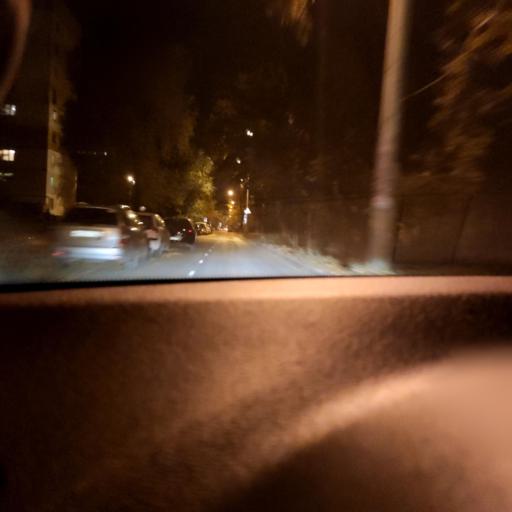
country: RU
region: Samara
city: Petra-Dubrava
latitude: 53.2277
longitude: 50.2716
